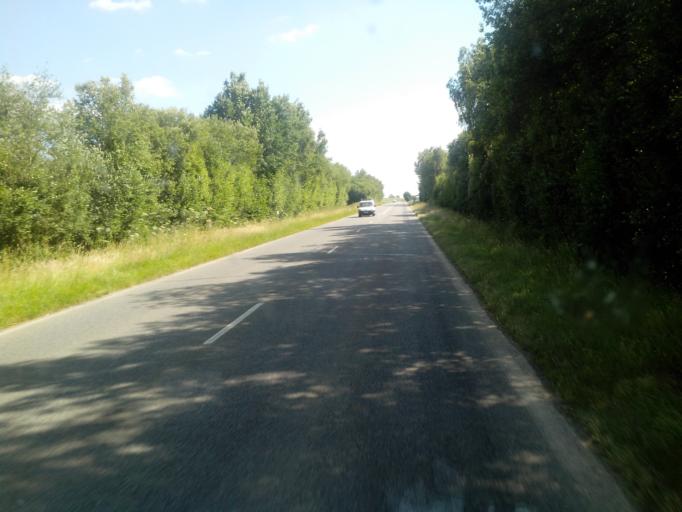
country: FR
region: Brittany
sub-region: Departement d'Ille-et-Vilaine
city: Acigne
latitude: 48.1423
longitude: -1.5164
